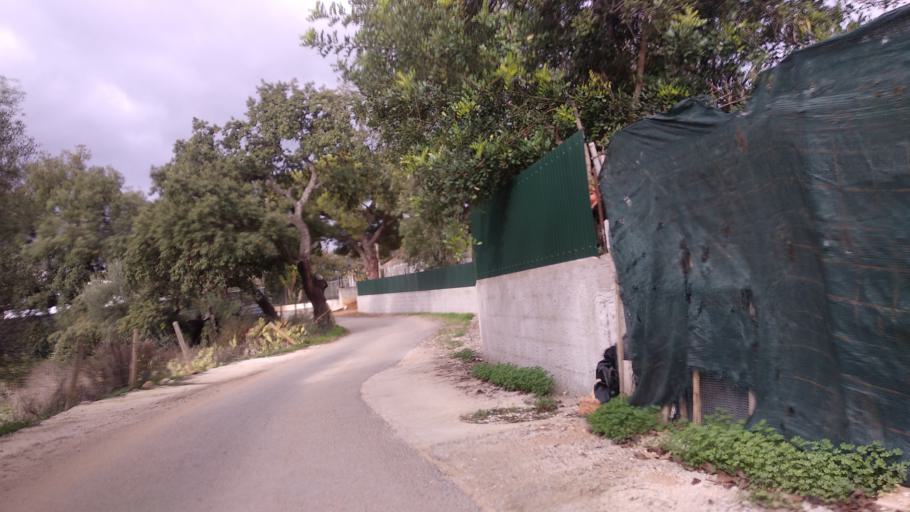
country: PT
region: Faro
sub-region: Loule
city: Almancil
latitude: 37.0986
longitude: -8.0466
